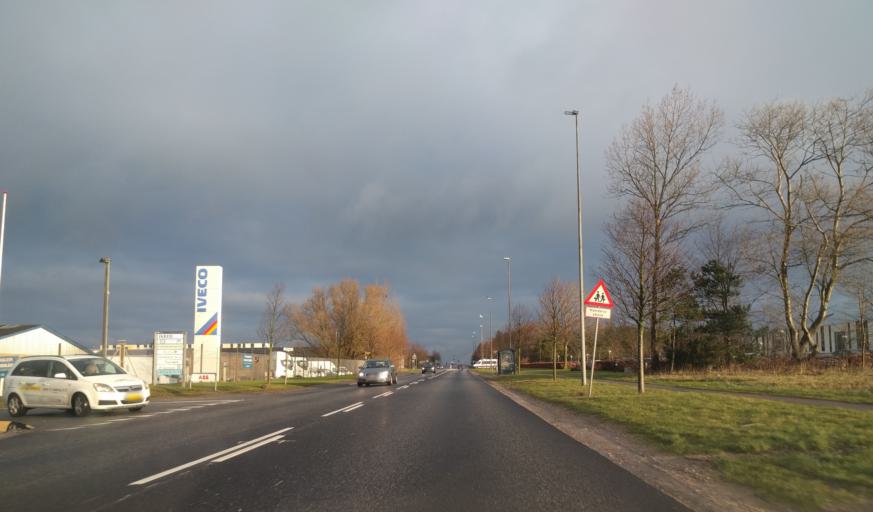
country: DK
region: North Denmark
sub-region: Alborg Kommune
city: Gistrup
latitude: 57.0266
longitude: 9.9761
